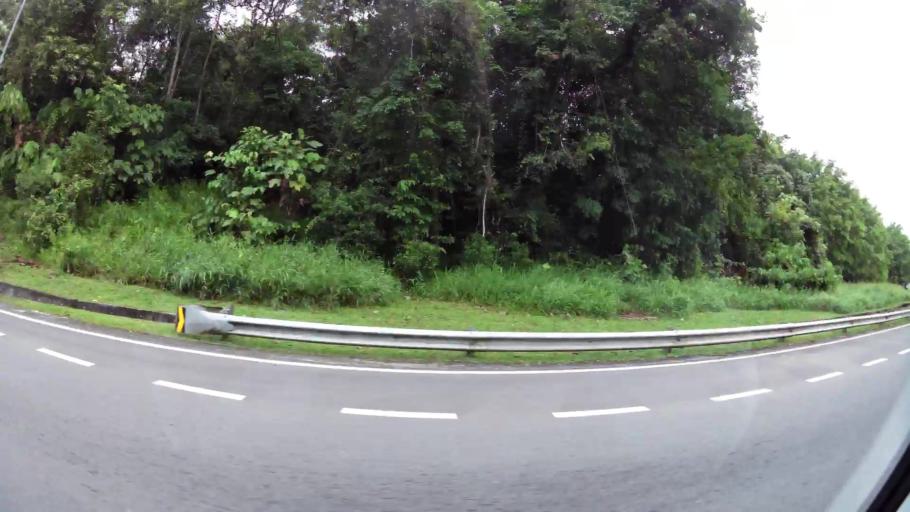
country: BN
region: Brunei and Muara
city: Bandar Seri Begawan
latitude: 4.9128
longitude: 114.9309
